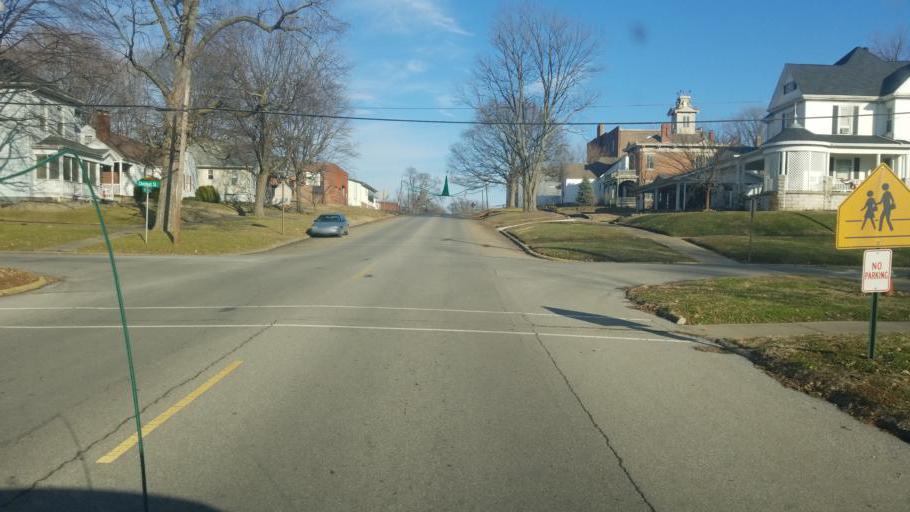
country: US
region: Illinois
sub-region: Wabash County
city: Mount Carmel
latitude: 38.4076
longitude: -87.7620
